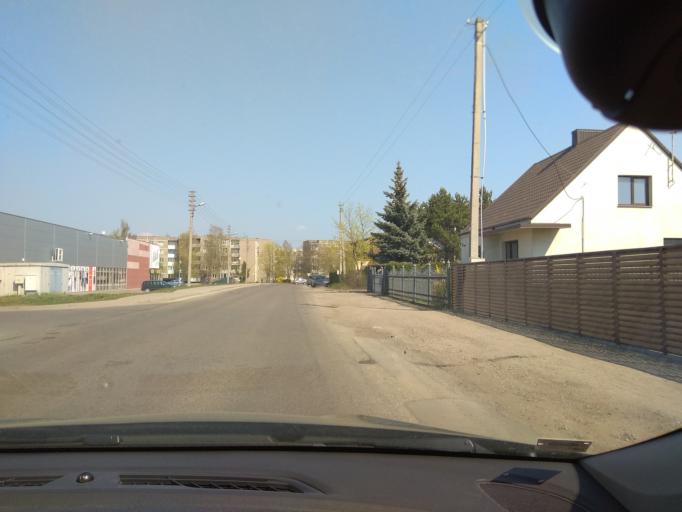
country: LT
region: Marijampoles apskritis
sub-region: Marijampole Municipality
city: Marijampole
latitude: 54.5661
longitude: 23.3505
